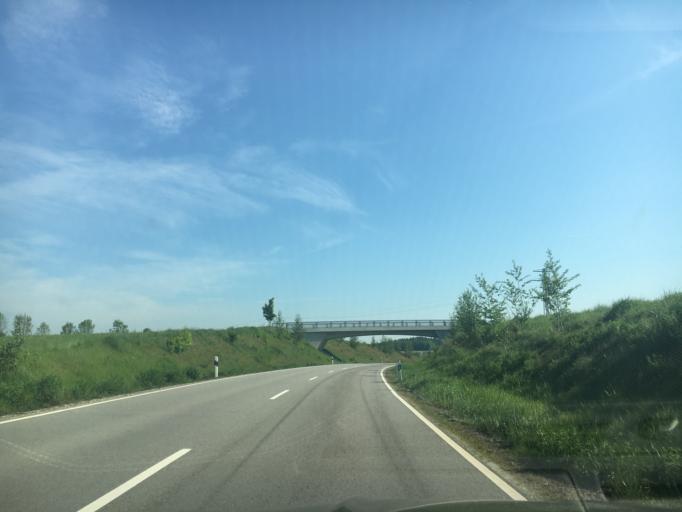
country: DE
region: Bavaria
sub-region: Upper Bavaria
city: Neumarkt-Sankt Veit
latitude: 48.3626
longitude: 12.4912
